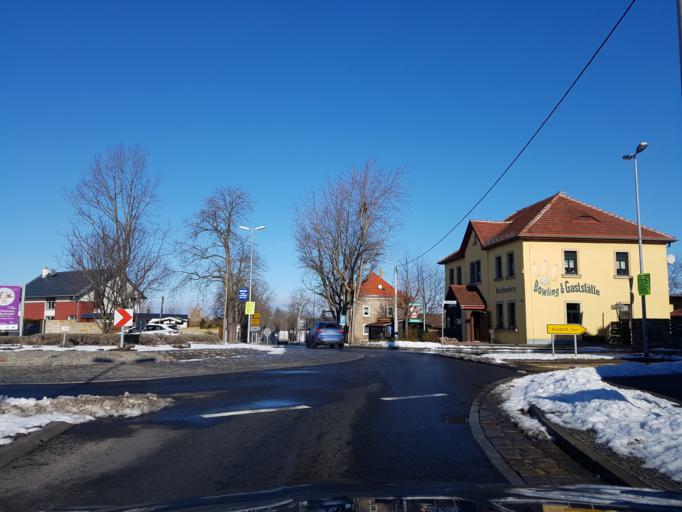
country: DE
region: Saxony
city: Radebeul
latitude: 51.1235
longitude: 13.6881
